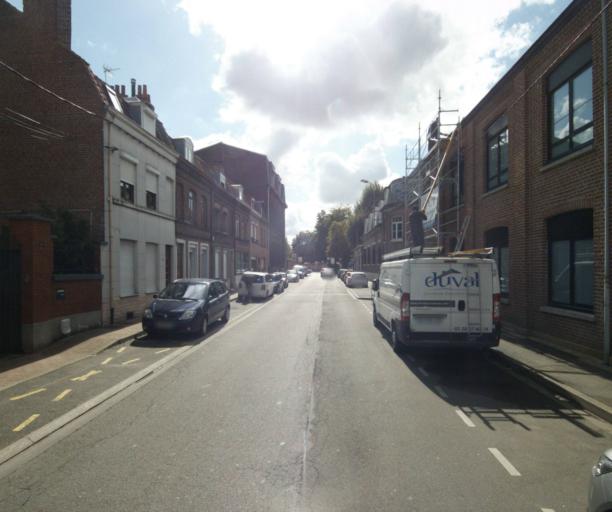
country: FR
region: Nord-Pas-de-Calais
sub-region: Departement du Nord
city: Loos
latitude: 50.6178
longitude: 3.0237
